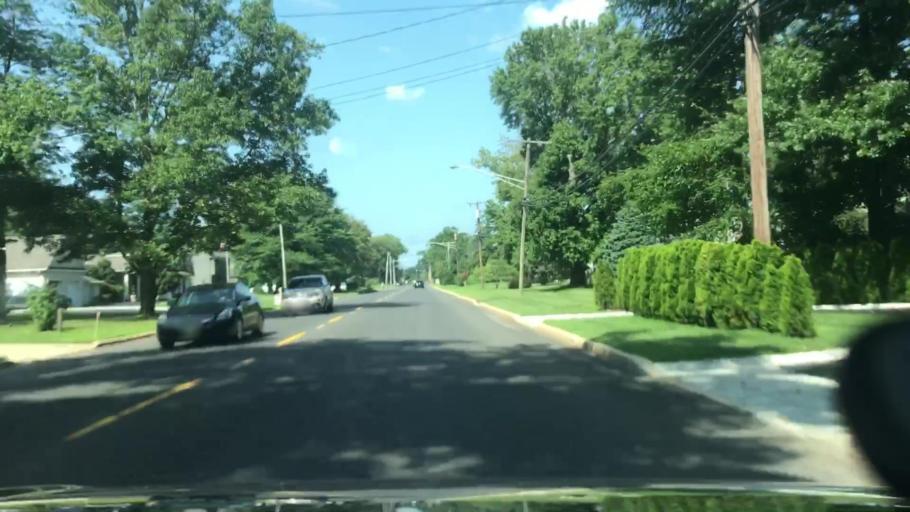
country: US
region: New Jersey
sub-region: Monmouth County
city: Oceanport
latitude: 40.3216
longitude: -74.0071
